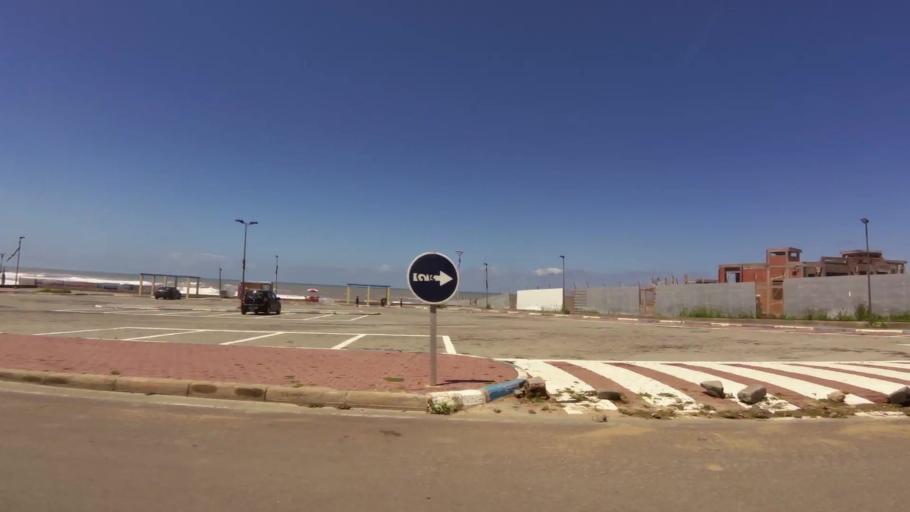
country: MA
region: Grand Casablanca
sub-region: Nouaceur
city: Dar Bouazza
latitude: 33.5297
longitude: -7.8303
